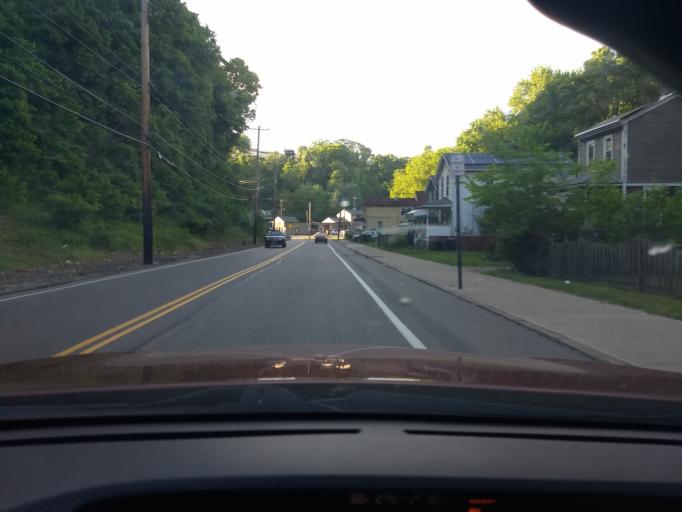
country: US
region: Pennsylvania
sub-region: Allegheny County
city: White Oak
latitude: 40.3537
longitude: -79.8343
